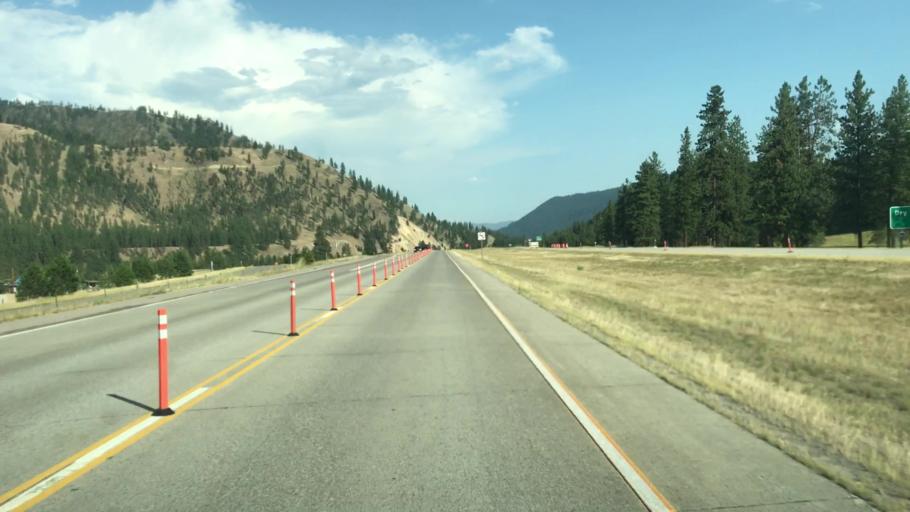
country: US
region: Montana
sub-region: Mineral County
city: Superior
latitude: 47.2291
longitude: -114.9752
